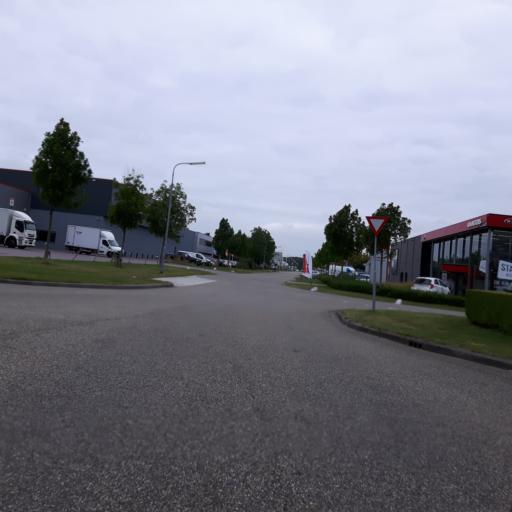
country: NL
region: Zeeland
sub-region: Gemeente Goes
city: Goes
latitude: 51.4856
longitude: 3.8764
